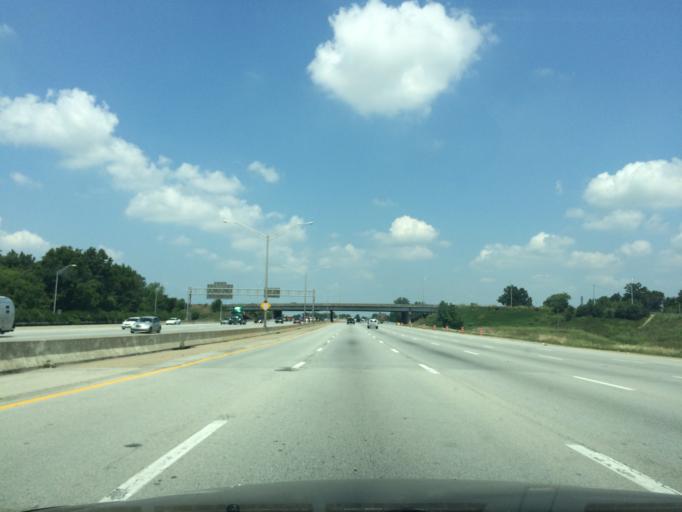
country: US
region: Kentucky
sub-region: Jefferson County
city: Heritage Creek
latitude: 38.1554
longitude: -85.7169
